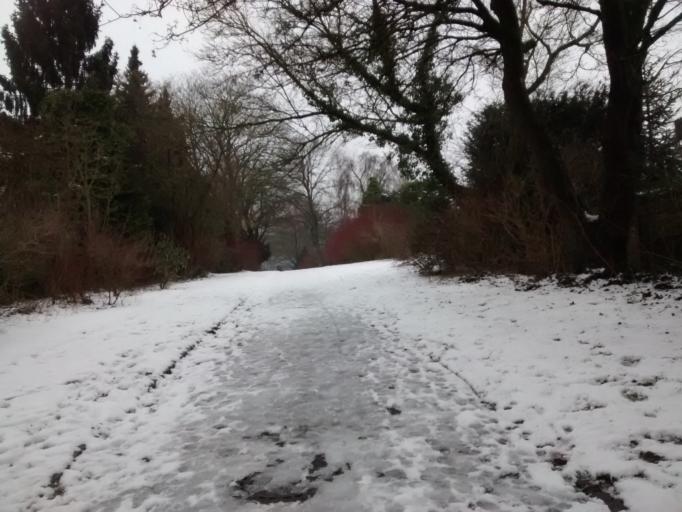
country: NL
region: Limburg
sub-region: Gemeente Vaals
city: Vaals
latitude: 50.7629
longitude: 6.0502
